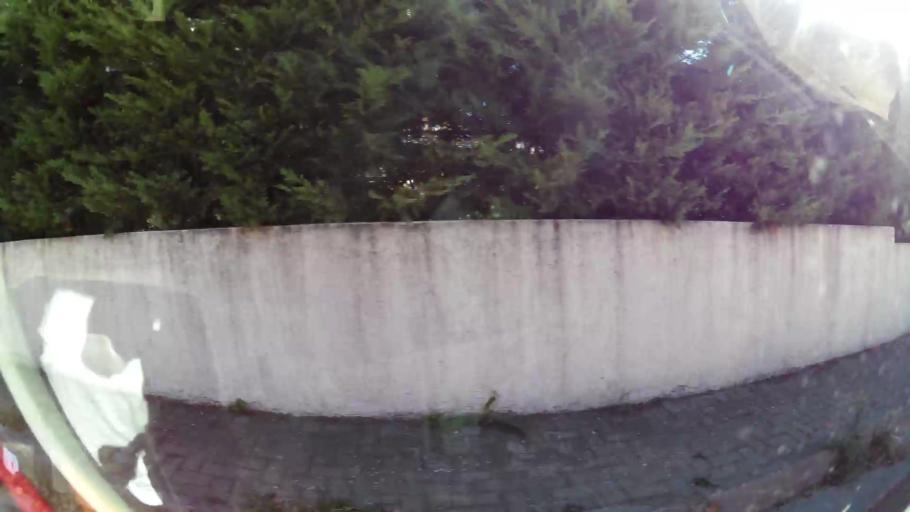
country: GR
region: Attica
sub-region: Nomarchia Anatolikis Attikis
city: Leondarion
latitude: 38.0002
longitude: 23.8592
